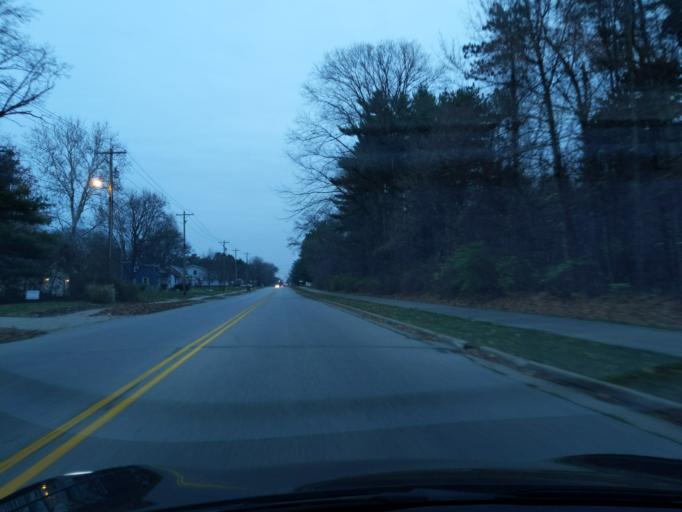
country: US
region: Indiana
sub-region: Saint Joseph County
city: Georgetown
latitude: 41.7304
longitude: -86.2625
